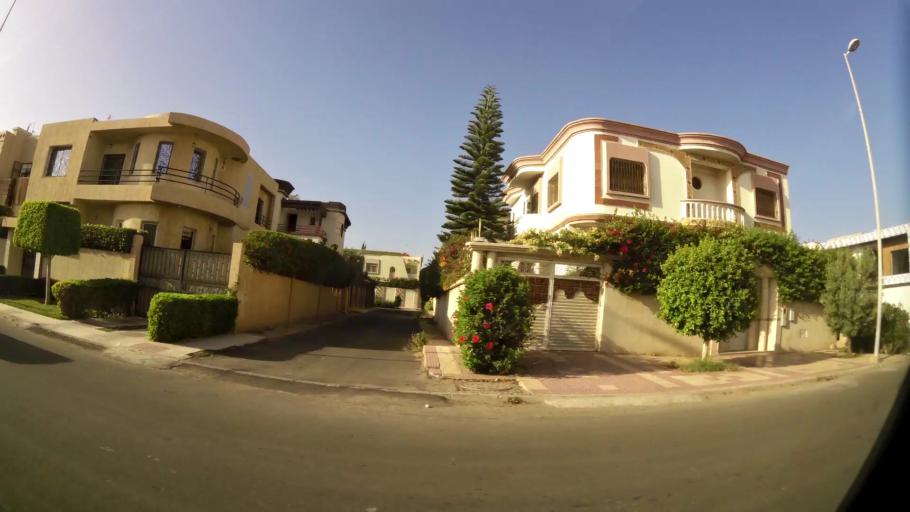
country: MA
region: Oued ed Dahab-Lagouira
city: Dakhla
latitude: 30.4012
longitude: -9.5398
